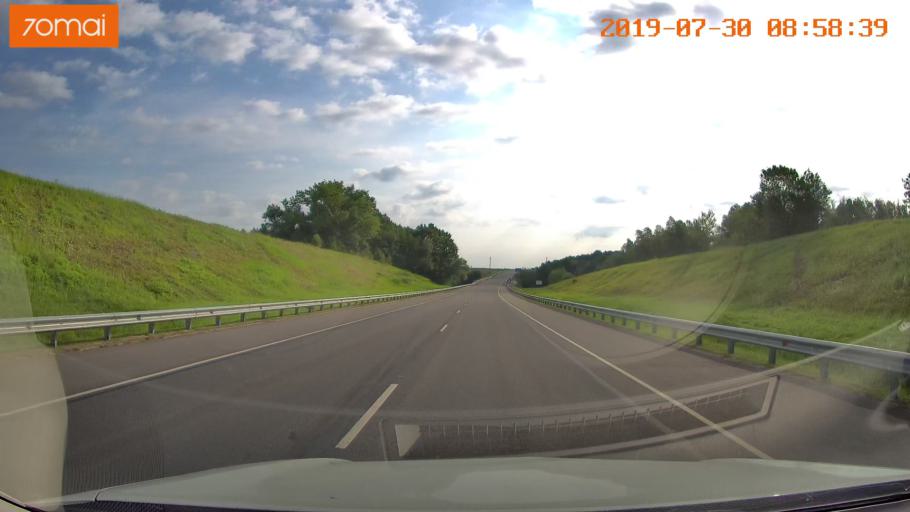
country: RU
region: Kaliningrad
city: Gusev
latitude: 54.6105
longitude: 22.1344
